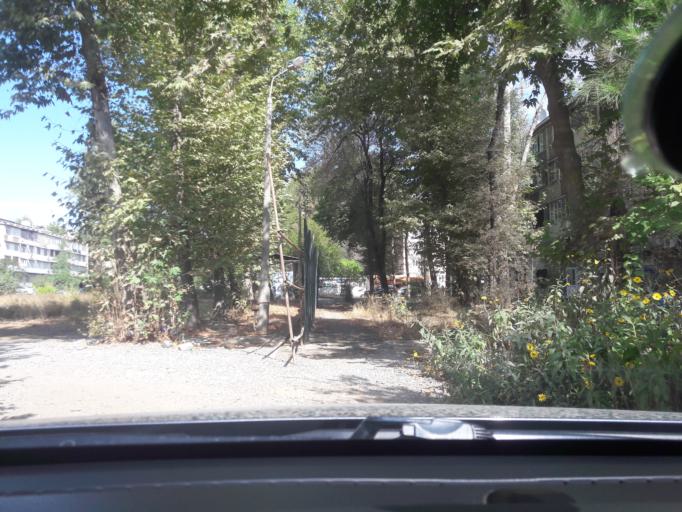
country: TJ
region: Dushanbe
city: Dushanbe
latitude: 38.5863
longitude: 68.7495
